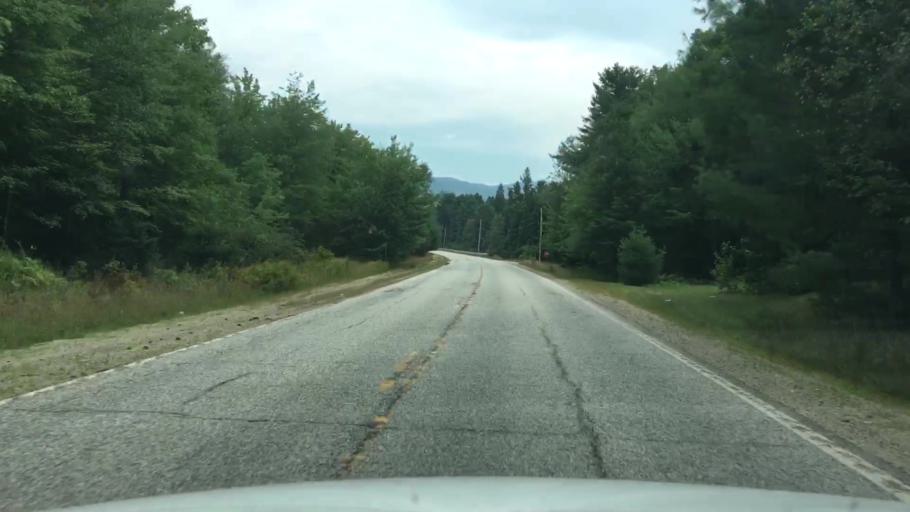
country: US
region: Maine
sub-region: Oxford County
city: Rumford
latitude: 44.5989
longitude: -70.7374
